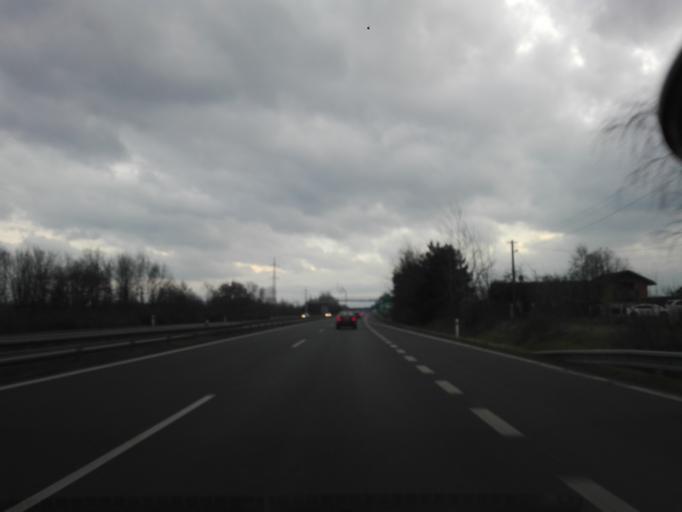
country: CZ
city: Paskov
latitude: 49.7485
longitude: 18.2785
